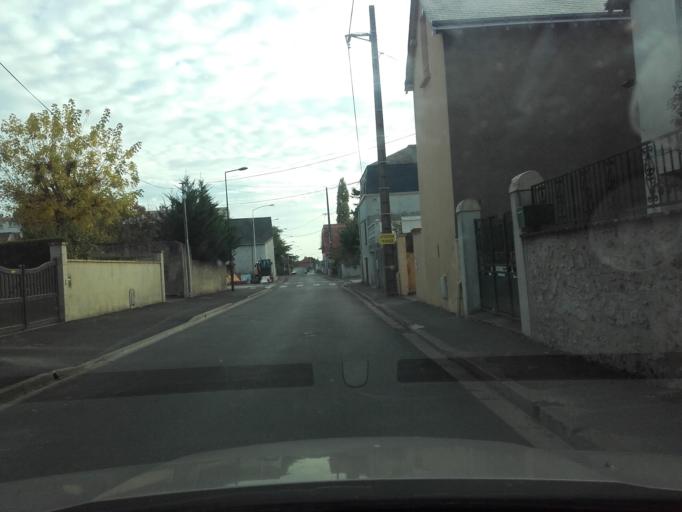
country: FR
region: Centre
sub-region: Departement d'Indre-et-Loire
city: Saint-Cyr-sur-Loire
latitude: 47.4147
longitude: 0.6968
